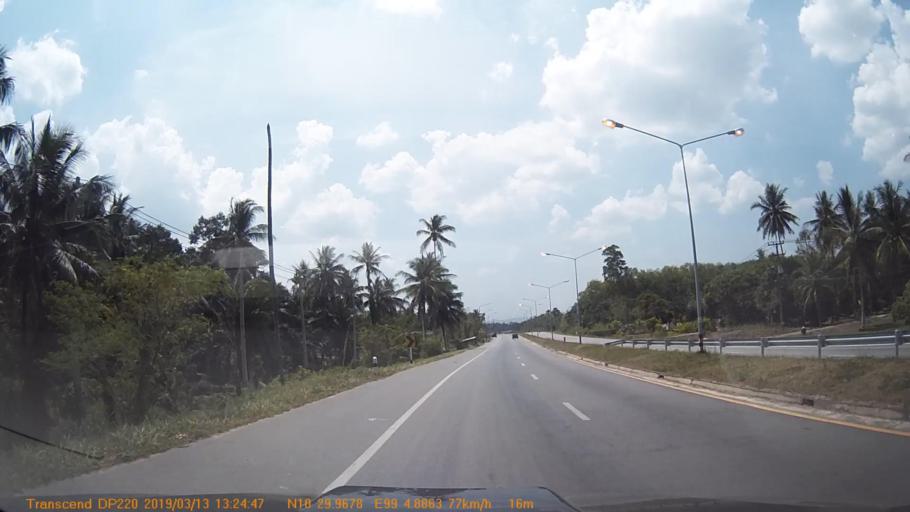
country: TH
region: Chumphon
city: Chumphon
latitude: 10.5013
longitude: 99.0853
